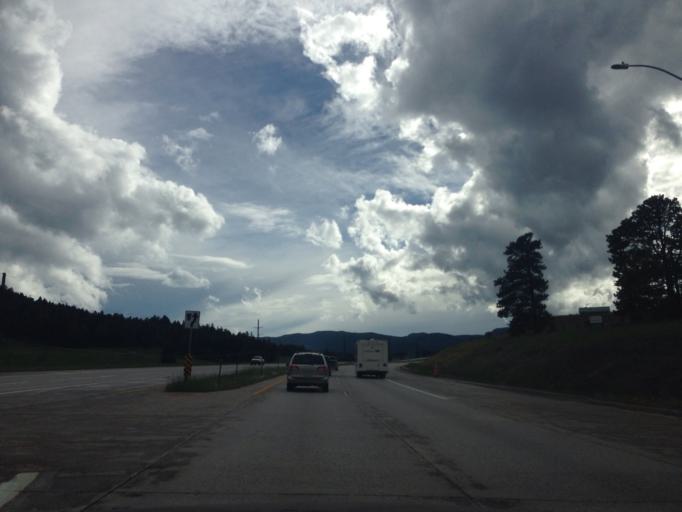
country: US
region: Colorado
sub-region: Jefferson County
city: Indian Hills
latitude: 39.5441
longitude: -105.2825
